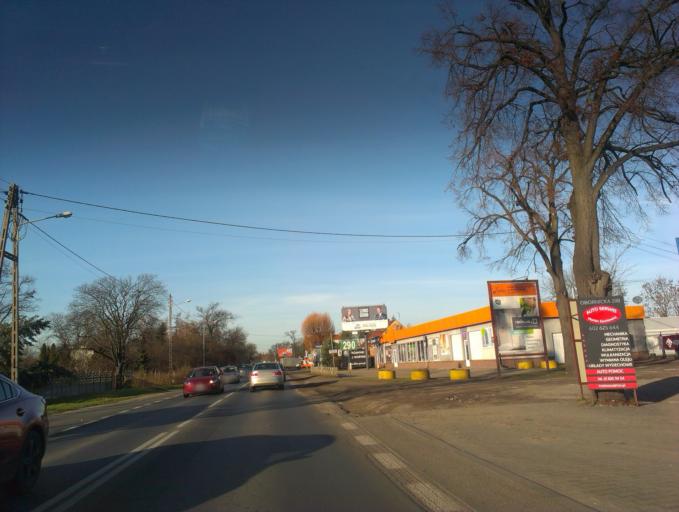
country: PL
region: Greater Poland Voivodeship
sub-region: Powiat poznanski
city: Suchy Las
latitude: 52.4517
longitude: 16.9041
